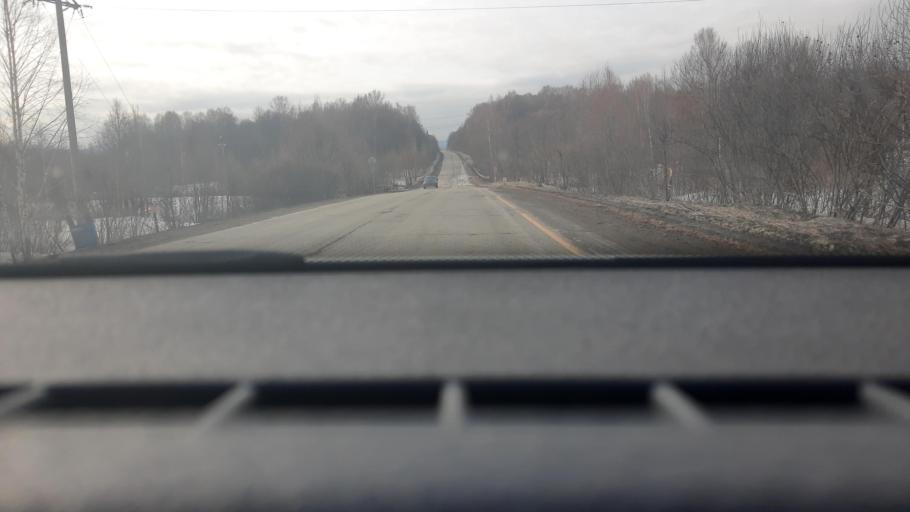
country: RU
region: Chelyabinsk
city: Asha
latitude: 54.9184
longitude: 57.2915
